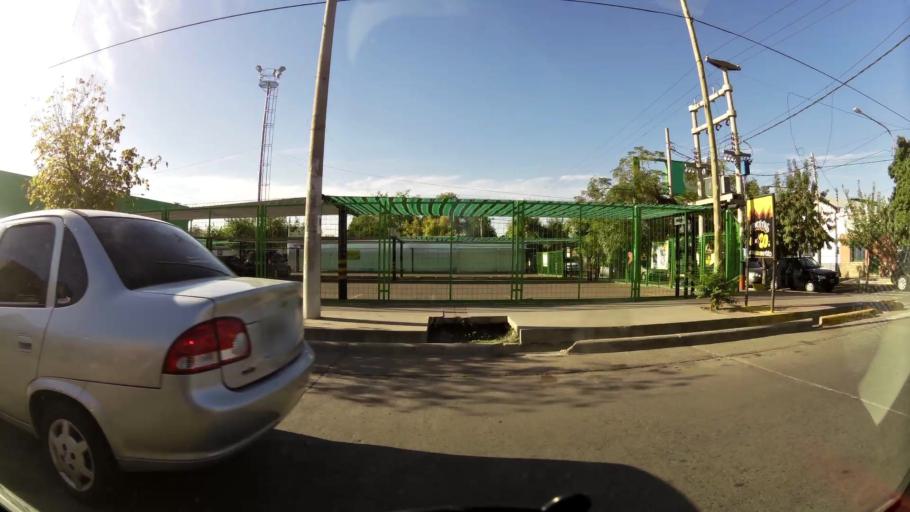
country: AR
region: Mendoza
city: Mendoza
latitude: -32.9031
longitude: -68.8329
